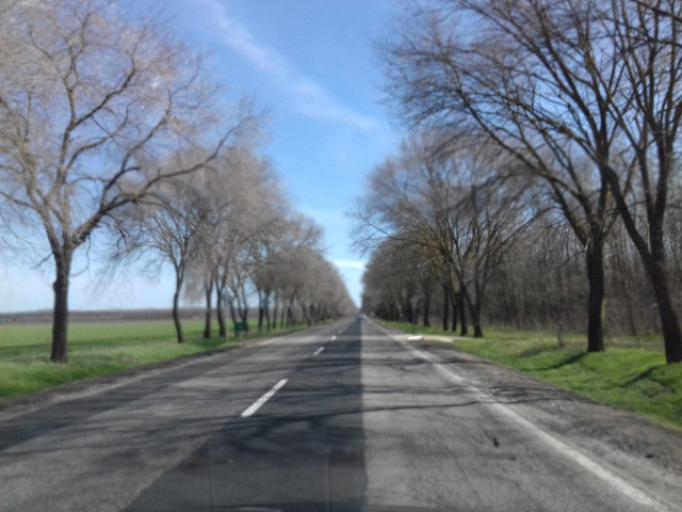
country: HU
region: Bacs-Kiskun
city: Nyarlorinc
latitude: 46.8996
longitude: 19.8204
